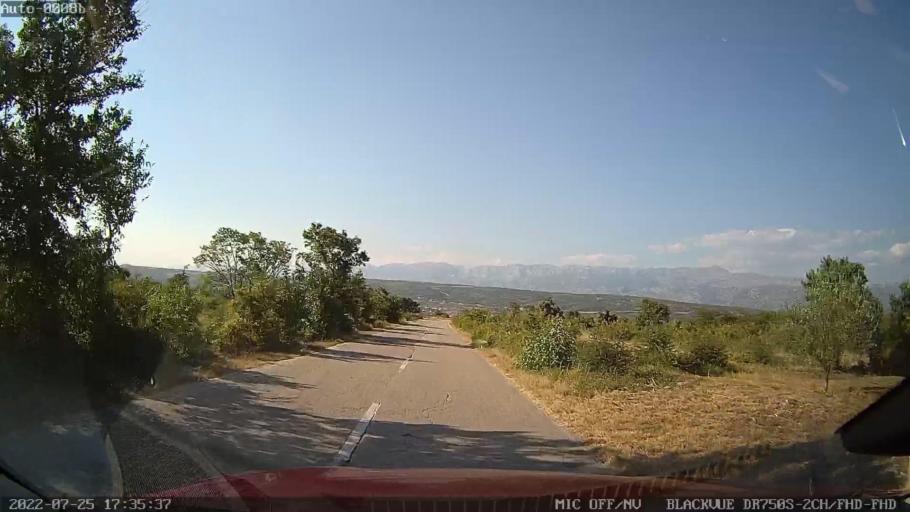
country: HR
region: Zadarska
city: Posedarje
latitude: 44.1923
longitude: 15.4725
